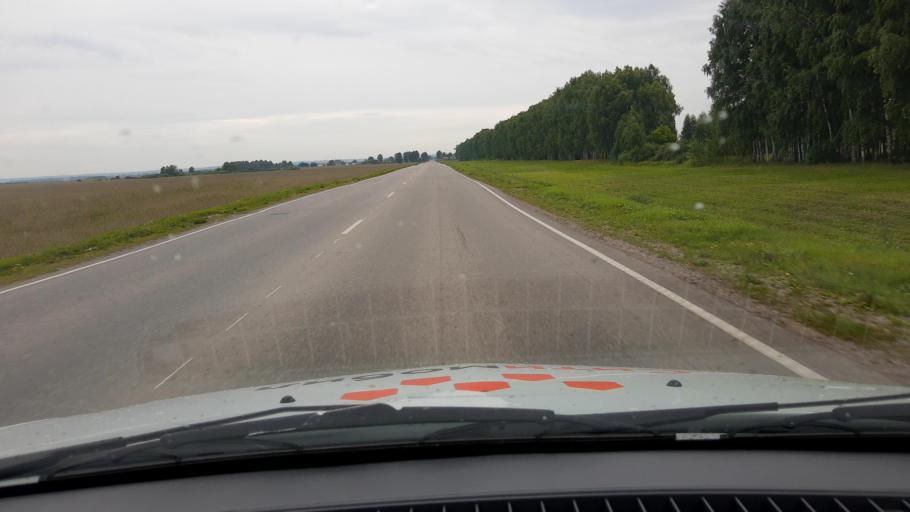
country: RU
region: Bashkortostan
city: Krasnaya Gorka
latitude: 55.1052
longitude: 56.6286
